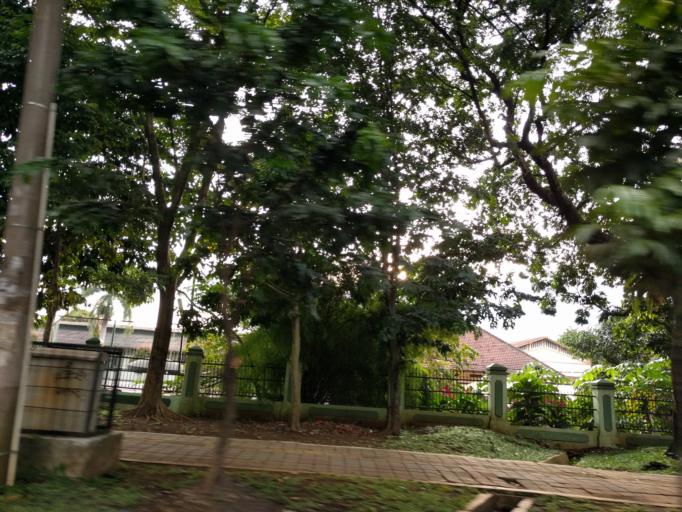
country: ID
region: West Java
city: Bogor
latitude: -6.5861
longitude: 106.7969
